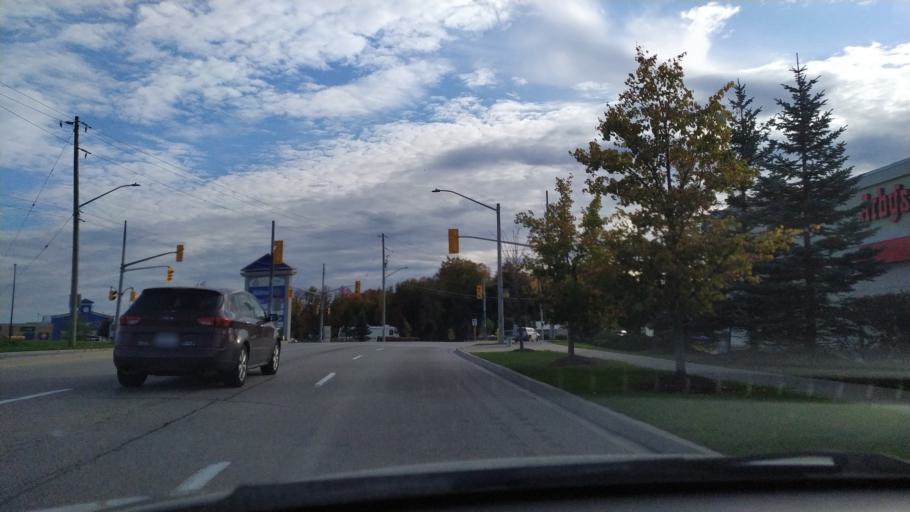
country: CA
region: Ontario
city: Waterloo
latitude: 43.5110
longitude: -80.5493
